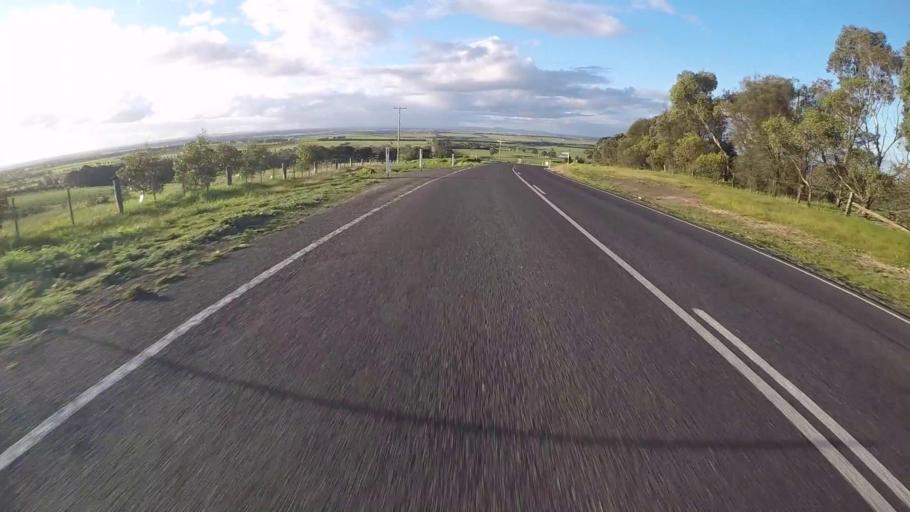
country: AU
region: Victoria
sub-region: Greater Geelong
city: Wandana Heights
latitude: -38.1568
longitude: 144.1629
